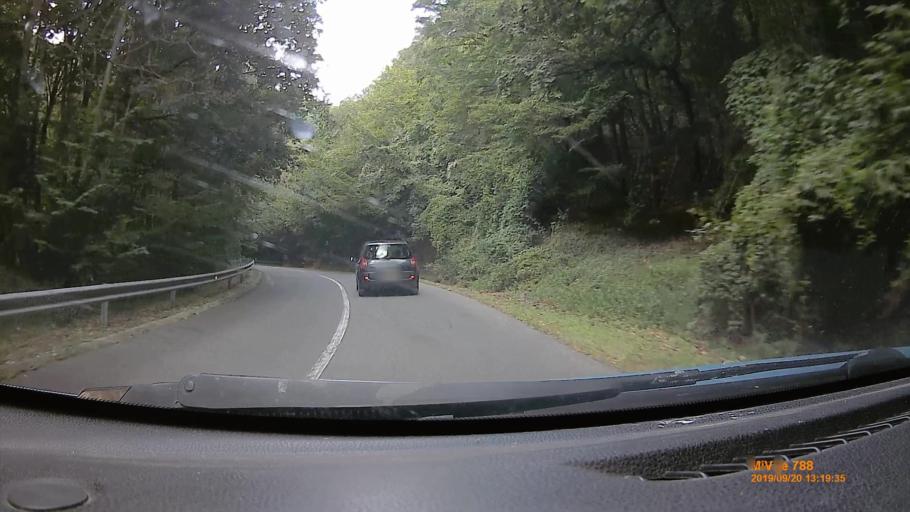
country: HU
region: Heves
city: Felsotarkany
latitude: 48.0084
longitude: 20.4651
